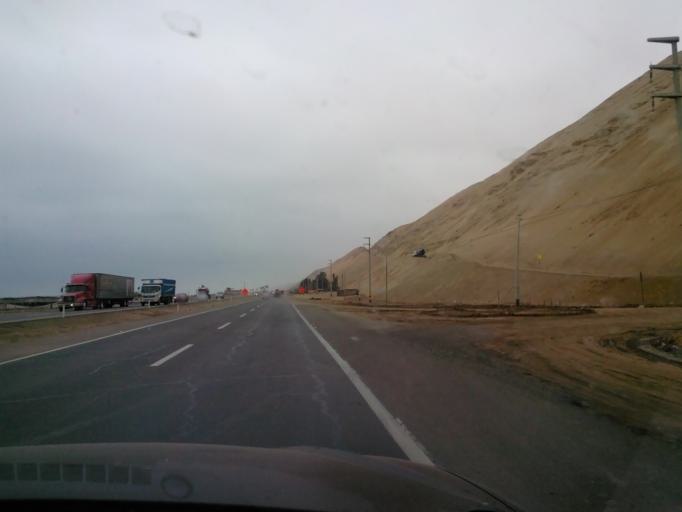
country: PE
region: Ica
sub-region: Provincia de Chincha
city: San Pedro
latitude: -13.3394
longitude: -76.2314
